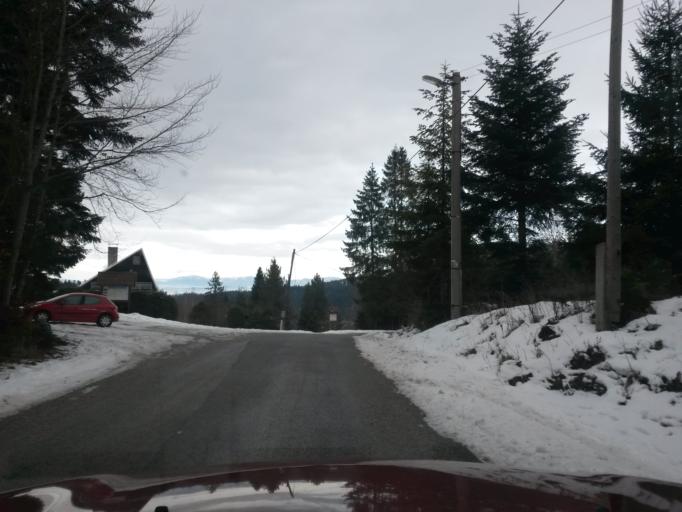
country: SK
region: Kosicky
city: Spisska Nova Ves
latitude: 48.8660
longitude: 20.5695
